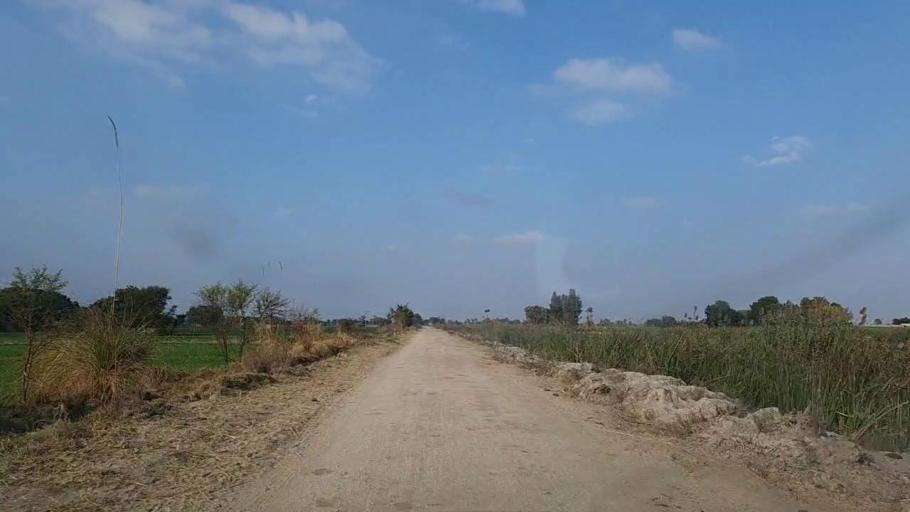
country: PK
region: Sindh
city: Sanghar
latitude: 26.2340
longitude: 68.9729
